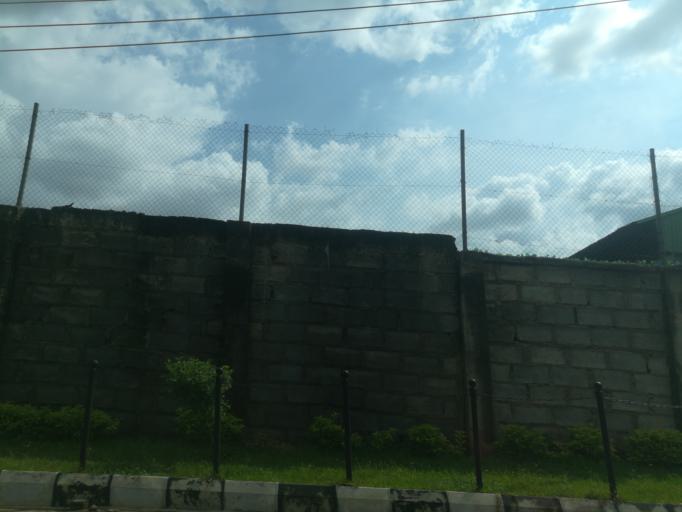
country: NG
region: Oyo
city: Ibadan
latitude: 7.3642
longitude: 3.8483
